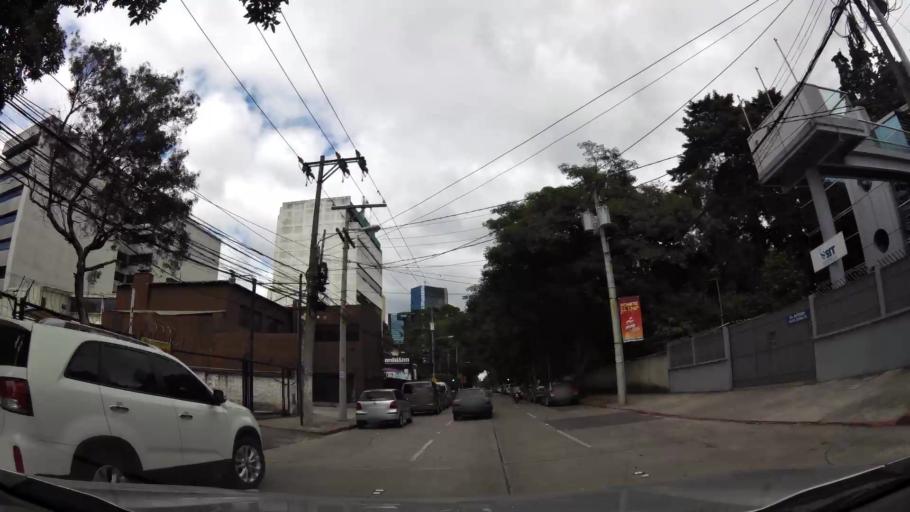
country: GT
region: Guatemala
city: Santa Catarina Pinula
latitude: 14.5956
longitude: -90.5135
